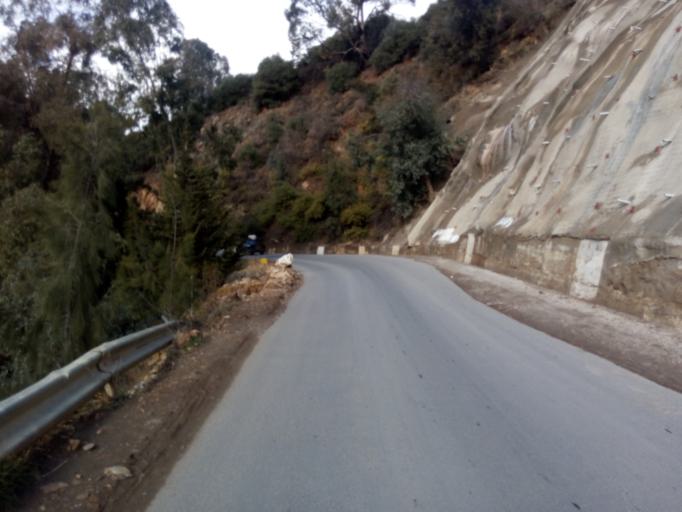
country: DZ
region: Tizi Ouzou
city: Chemini
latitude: 36.6068
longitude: 4.6436
